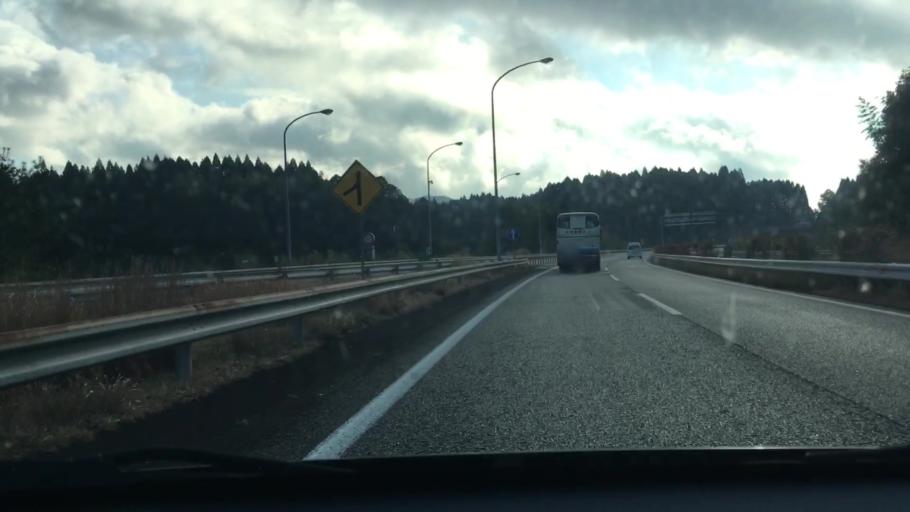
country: JP
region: Kagoshima
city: Okuchi-shinohara
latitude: 32.0289
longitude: 130.7968
